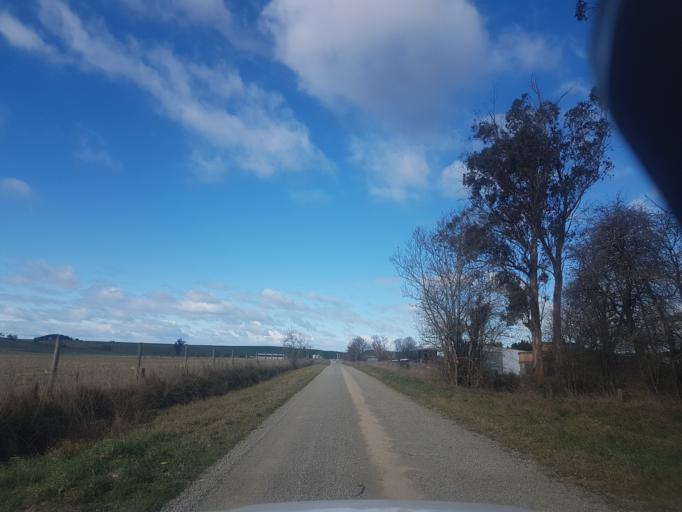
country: NZ
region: Canterbury
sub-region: Timaru District
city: Pleasant Point
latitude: -44.1887
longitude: 171.1946
